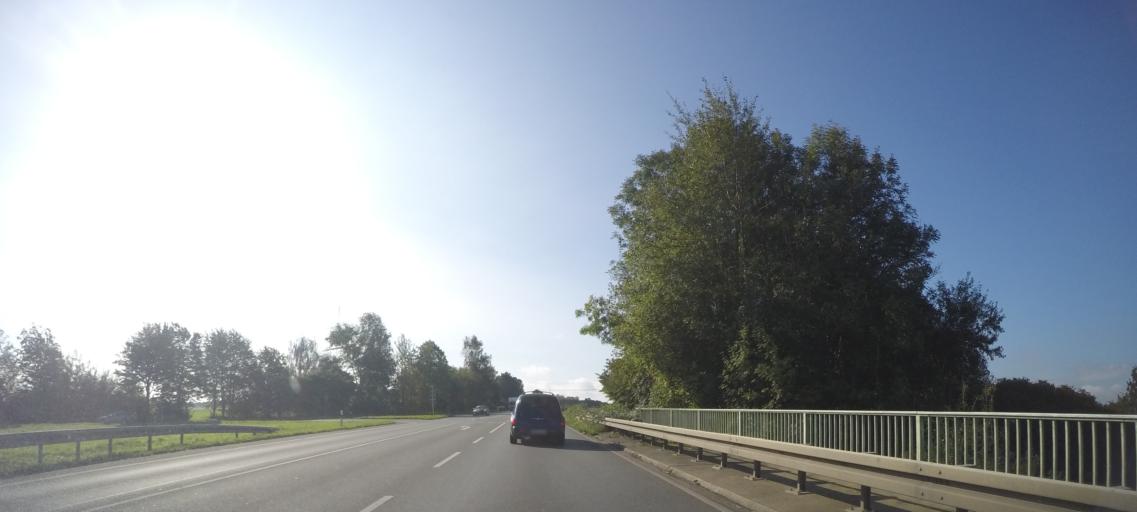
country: DE
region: North Rhine-Westphalia
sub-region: Regierungsbezirk Arnsberg
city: Unna
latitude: 51.5070
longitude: 7.7015
